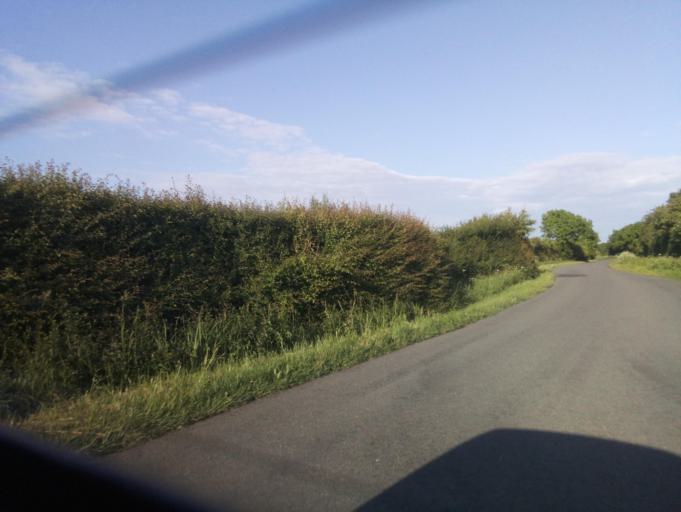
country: GB
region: England
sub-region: Lincolnshire
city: Navenby
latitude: 53.1138
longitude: -0.6057
